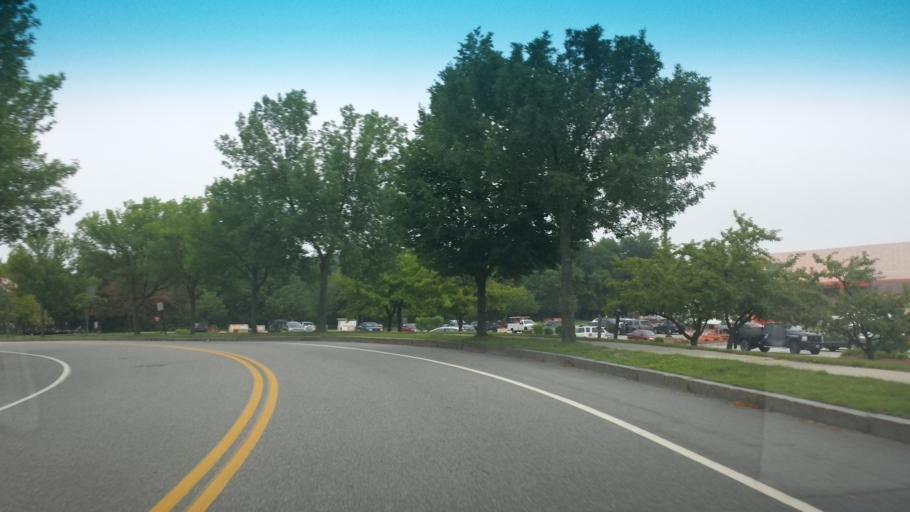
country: US
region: Maine
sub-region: Cumberland County
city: South Portland Gardens
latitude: 43.6313
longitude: -70.3220
